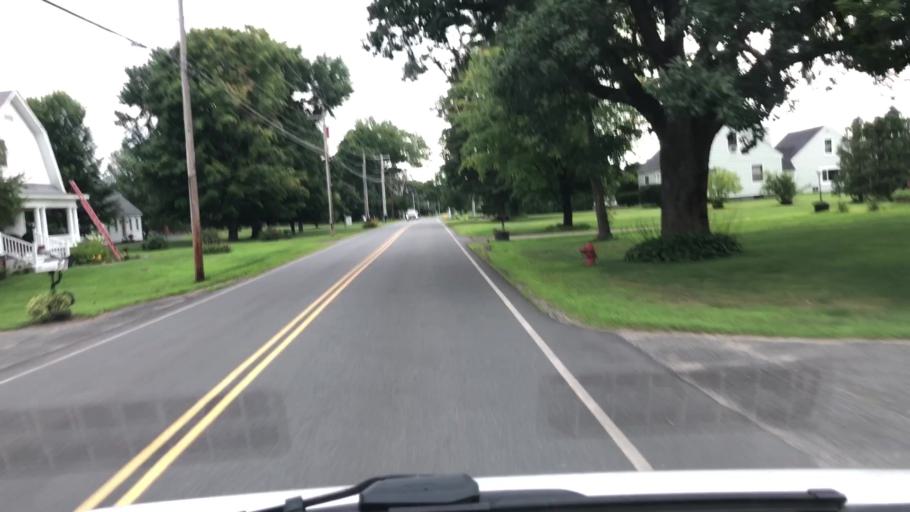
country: US
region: Massachusetts
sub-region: Franklin County
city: Whately
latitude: 42.4457
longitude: -72.6134
